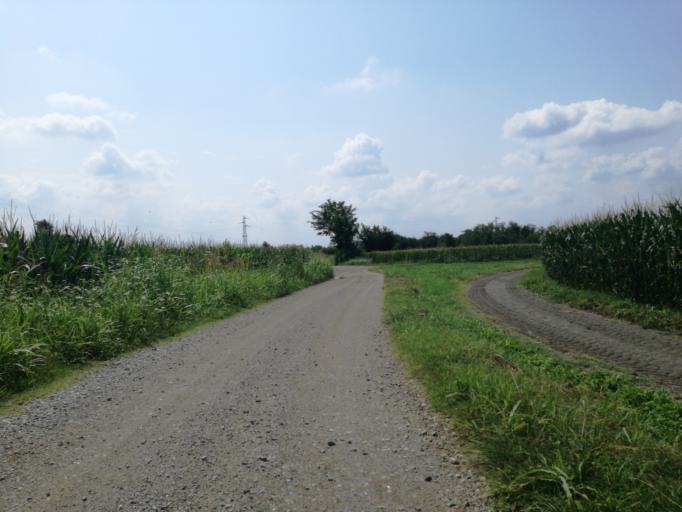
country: IT
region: Lombardy
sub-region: Provincia di Bergamo
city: Calusco d'Adda
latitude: 45.6792
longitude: 9.4748
